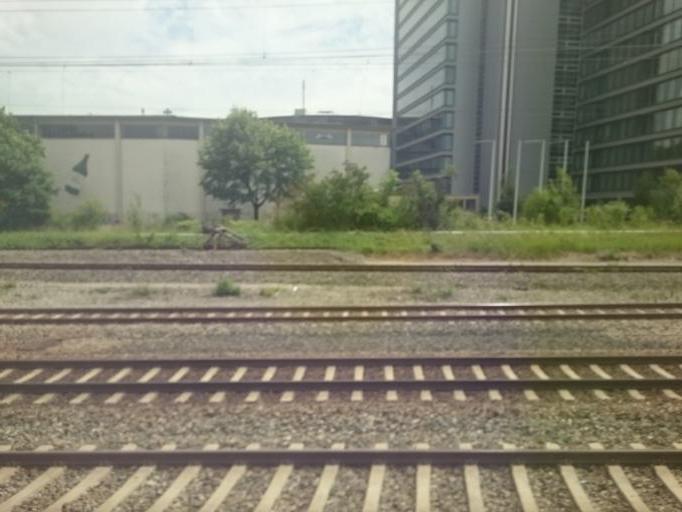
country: DE
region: Bavaria
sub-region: Upper Bavaria
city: Bogenhausen
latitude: 48.1337
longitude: 11.6148
